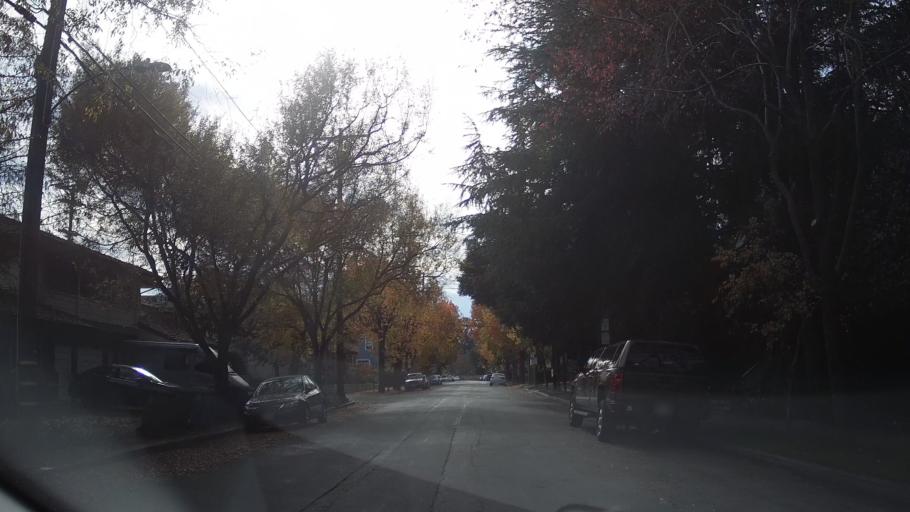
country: US
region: California
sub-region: San Mateo County
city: Menlo Park
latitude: 37.4481
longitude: -122.1656
